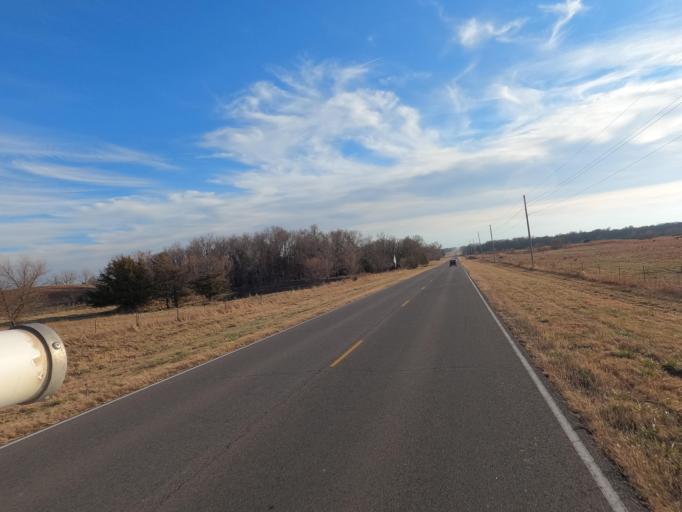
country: US
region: Kansas
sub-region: Reno County
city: Buhler
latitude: 38.0490
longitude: -97.7753
